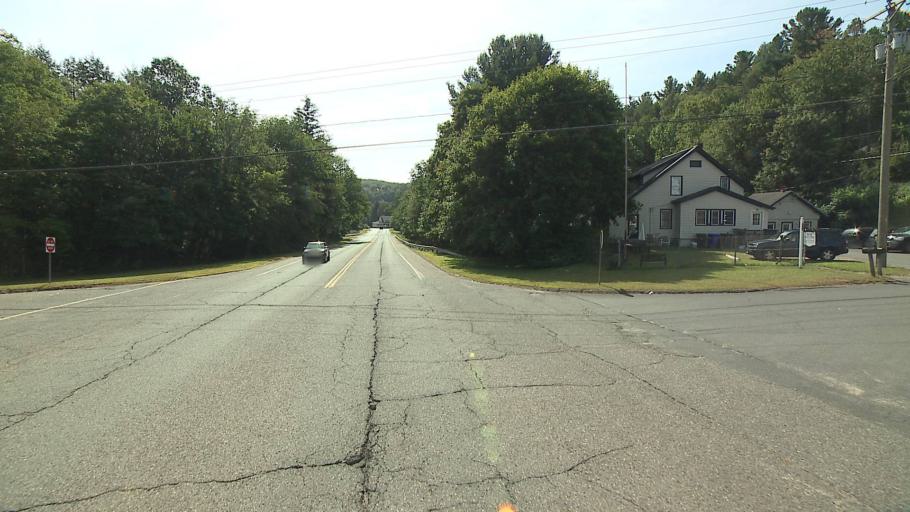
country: US
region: Connecticut
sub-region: Litchfield County
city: Thomaston
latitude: 41.6706
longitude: -73.0814
